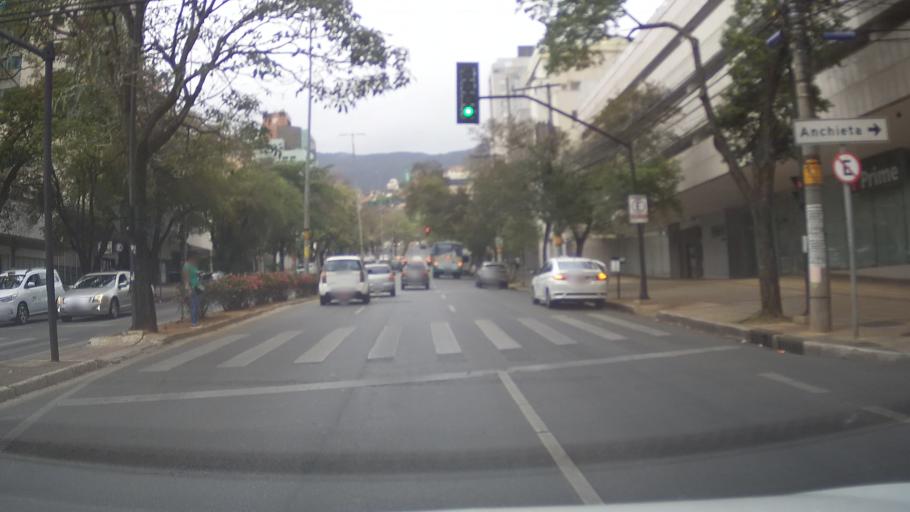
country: BR
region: Minas Gerais
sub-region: Belo Horizonte
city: Belo Horizonte
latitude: -19.9456
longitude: -43.9222
